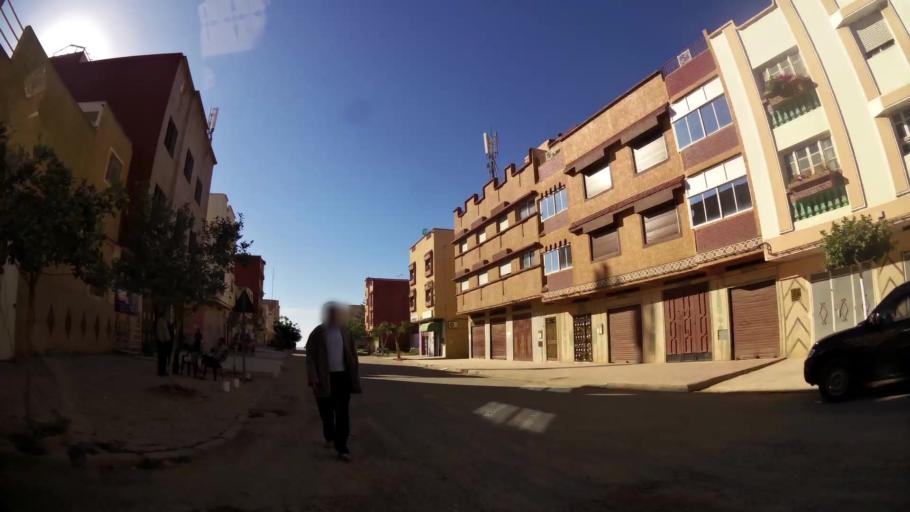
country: MA
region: Oriental
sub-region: Berkane-Taourirt
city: Ahfir
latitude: 34.9564
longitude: -2.1040
